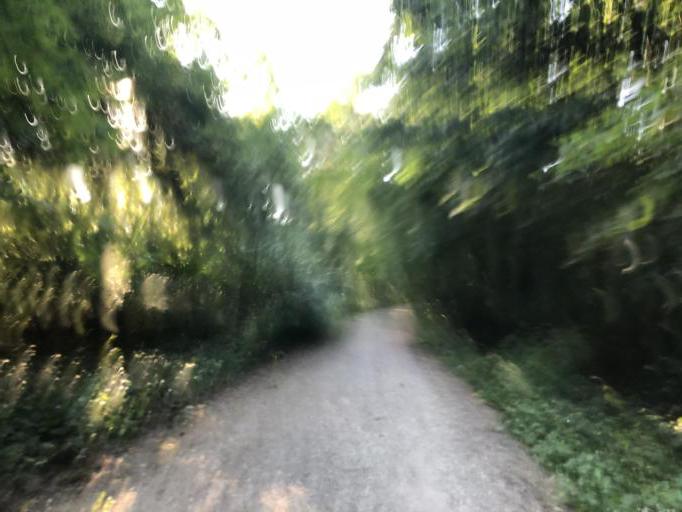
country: DE
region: Bavaria
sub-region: Regierungsbezirk Mittelfranken
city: Kalchreuth
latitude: 49.5479
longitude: 11.1053
